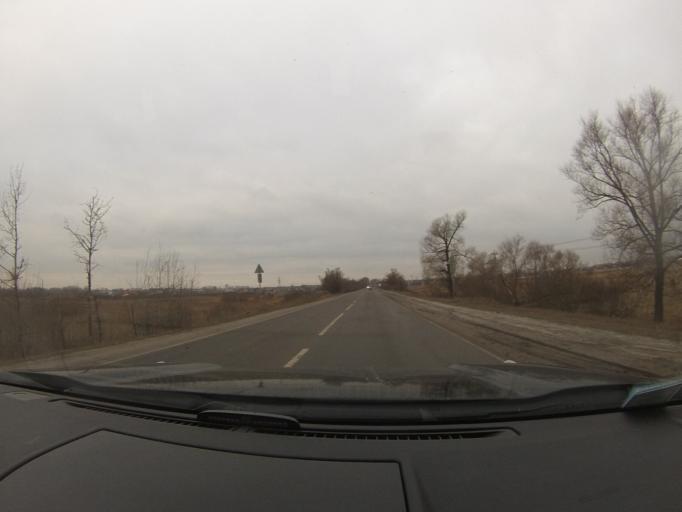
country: RU
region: Moskovskaya
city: Lopatinskiy
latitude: 55.3267
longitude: 38.7315
